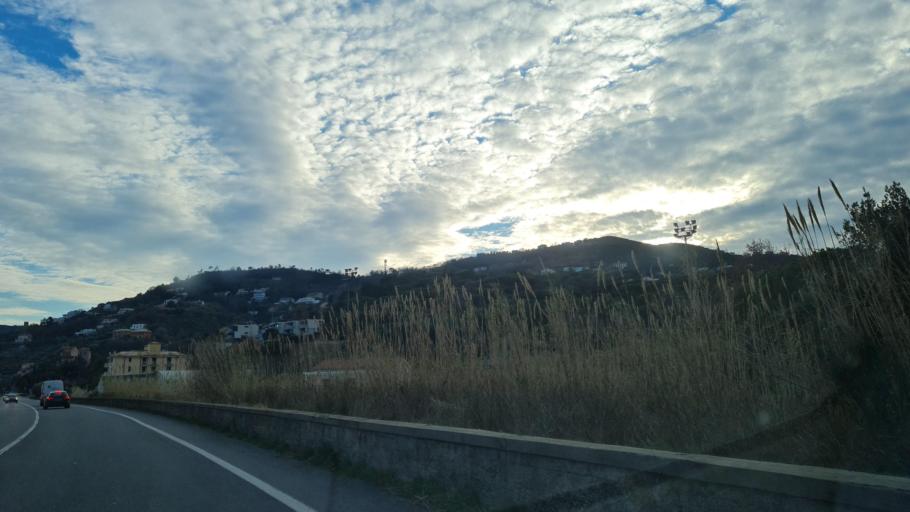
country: IT
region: Liguria
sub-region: Provincia di Savona
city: Spotorno
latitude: 44.2234
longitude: 8.4142
